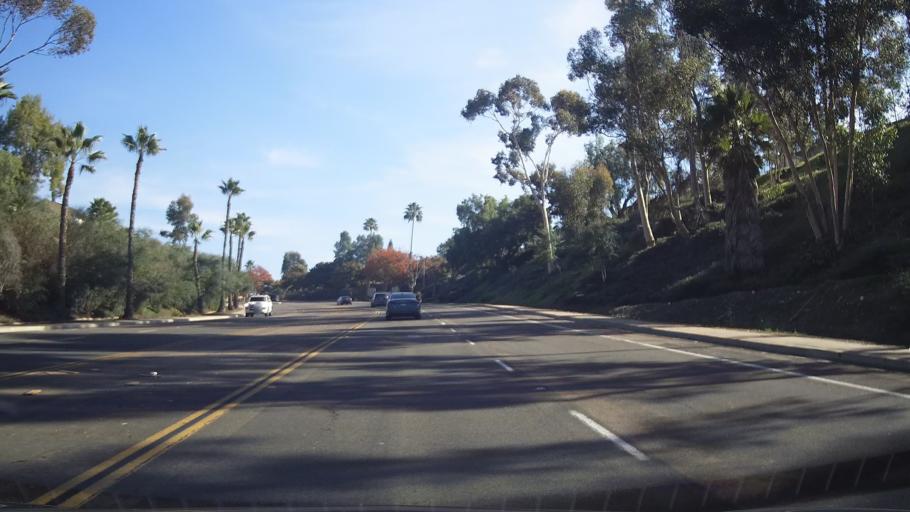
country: US
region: California
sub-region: San Diego County
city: La Mesa
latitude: 32.8104
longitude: -117.1084
